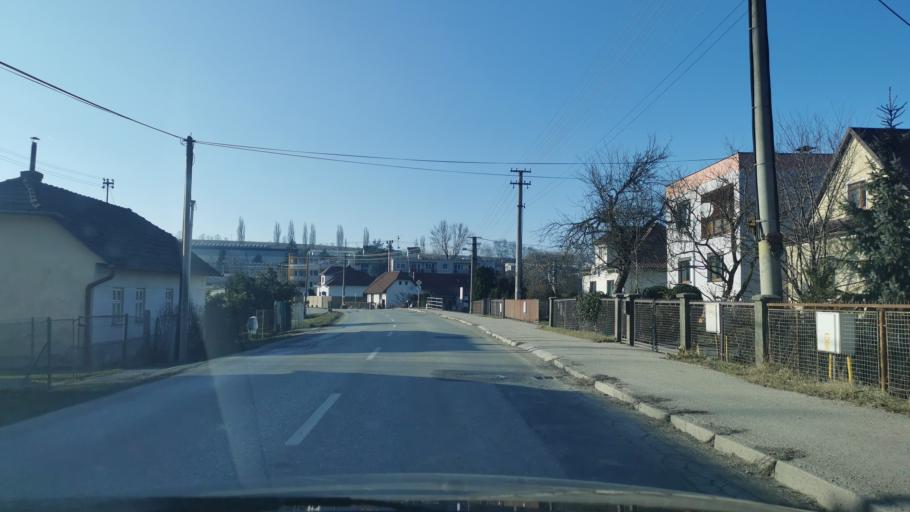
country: SK
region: Trenciansky
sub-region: Okres Myjava
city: Myjava
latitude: 48.7476
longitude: 17.5489
